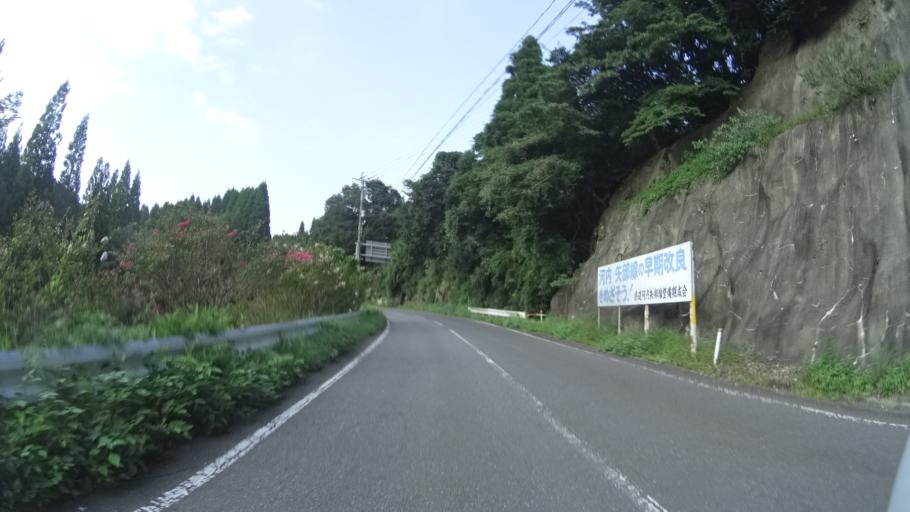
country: JP
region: Kumamoto
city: Ozu
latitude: 32.6865
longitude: 131.0112
